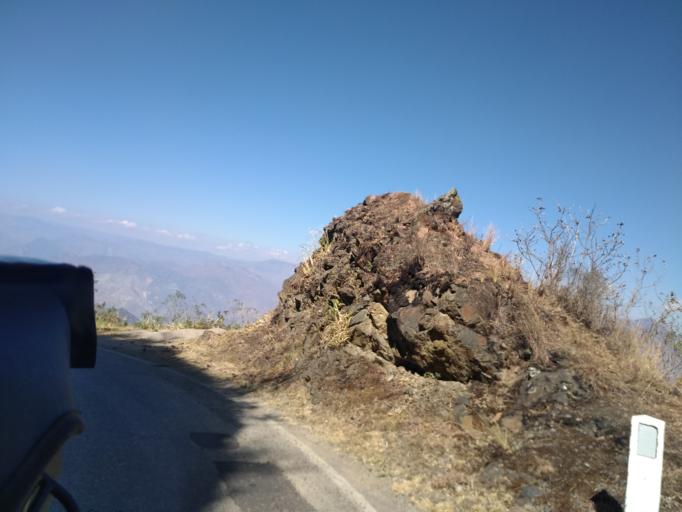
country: PE
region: Amazonas
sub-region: Provincia de Chachapoyas
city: Balsas
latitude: -6.7944
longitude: -77.9433
